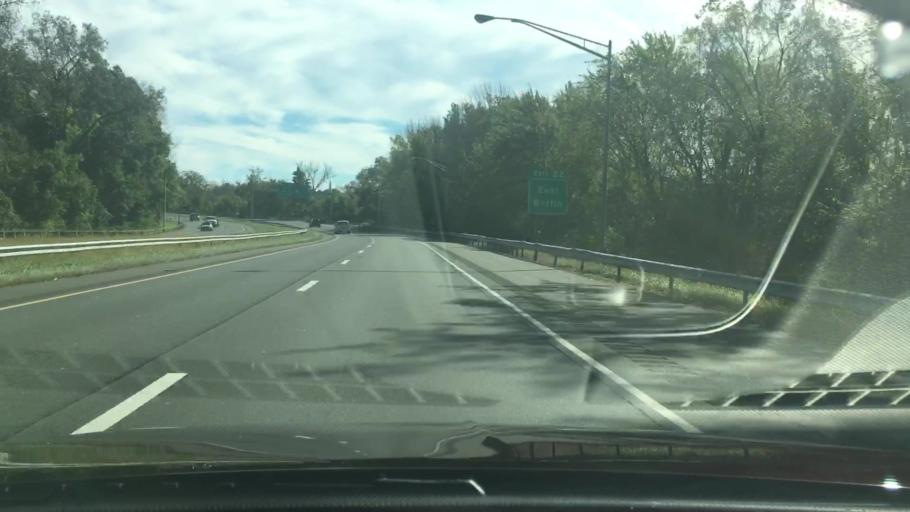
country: US
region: Connecticut
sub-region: Hartford County
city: Kensington
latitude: 41.6313
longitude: -72.7517
